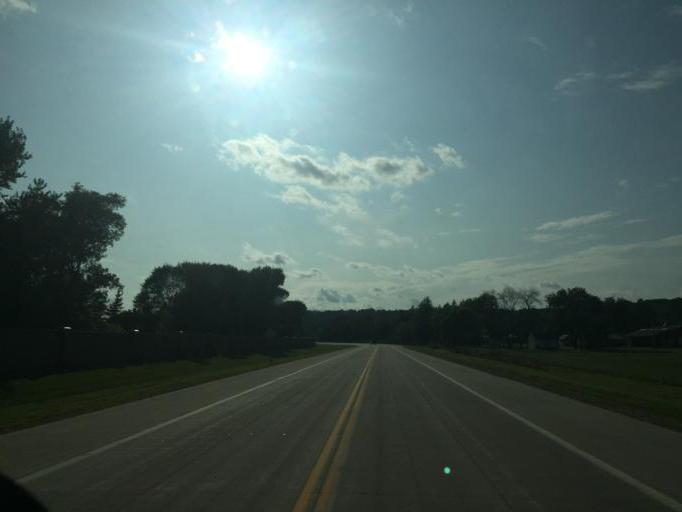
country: US
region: Minnesota
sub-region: Olmsted County
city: Rochester
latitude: 44.0037
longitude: -92.5107
